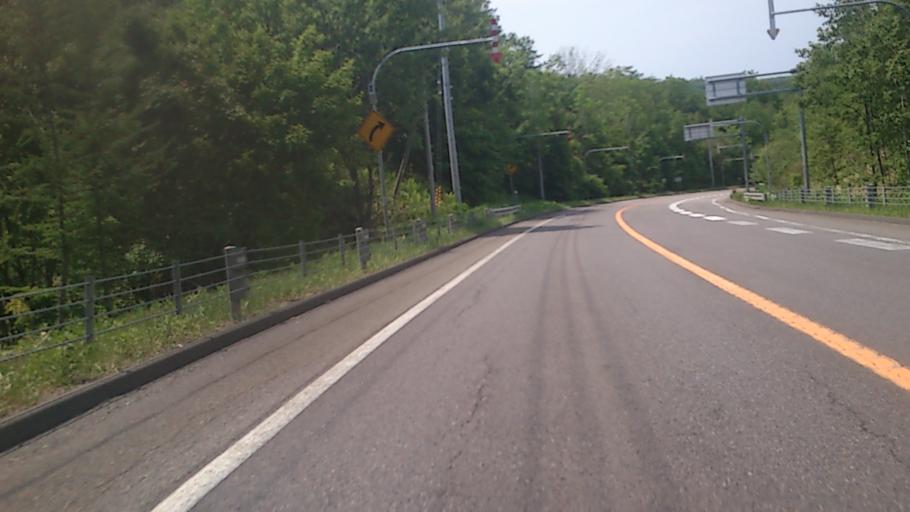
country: JP
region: Hokkaido
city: Otofuke
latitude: 43.2289
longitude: 143.5283
